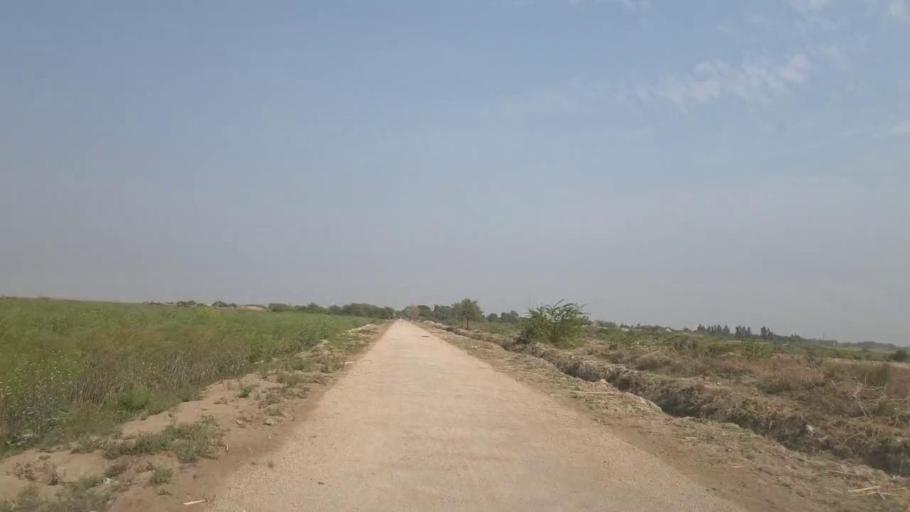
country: PK
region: Sindh
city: Mirpur Khas
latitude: 25.5861
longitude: 69.1393
